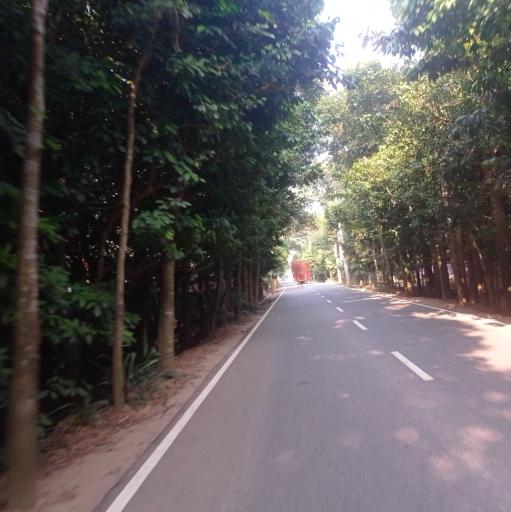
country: BD
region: Dhaka
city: Bhairab Bazar
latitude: 24.0585
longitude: 90.8382
